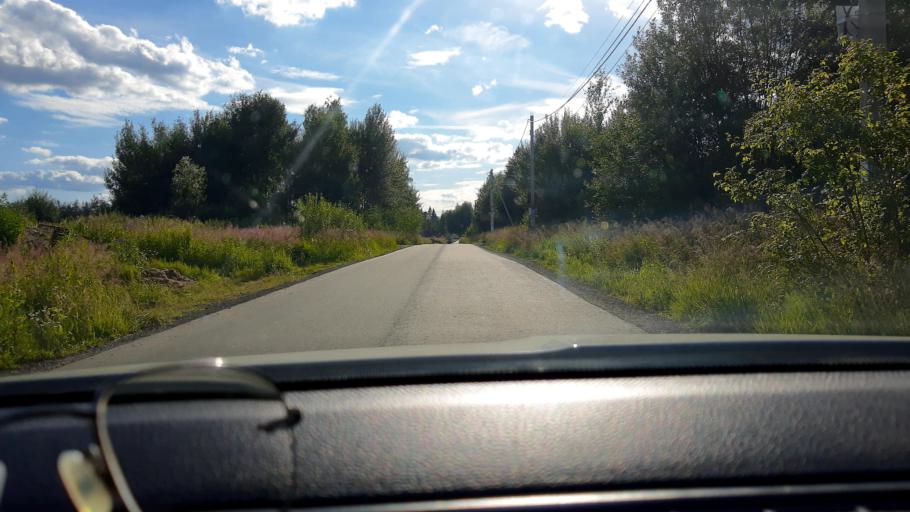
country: RU
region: Moskovskaya
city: Nazar'yevo
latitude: 55.6920
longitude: 37.0553
